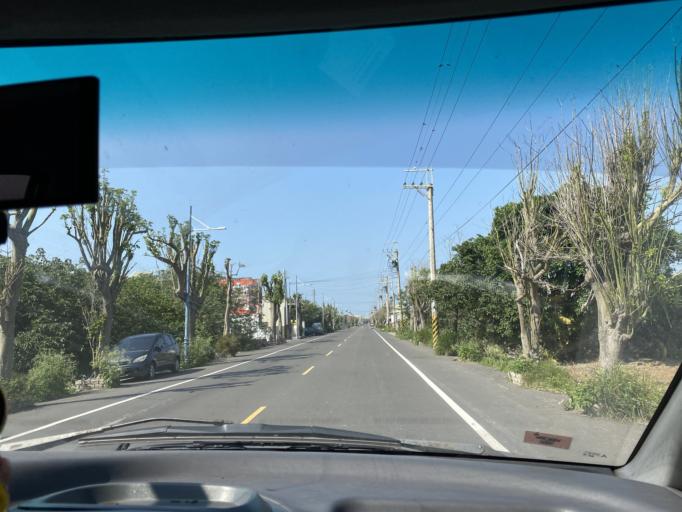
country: TW
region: Taiwan
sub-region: Changhua
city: Chang-hua
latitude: 23.9548
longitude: 120.3346
